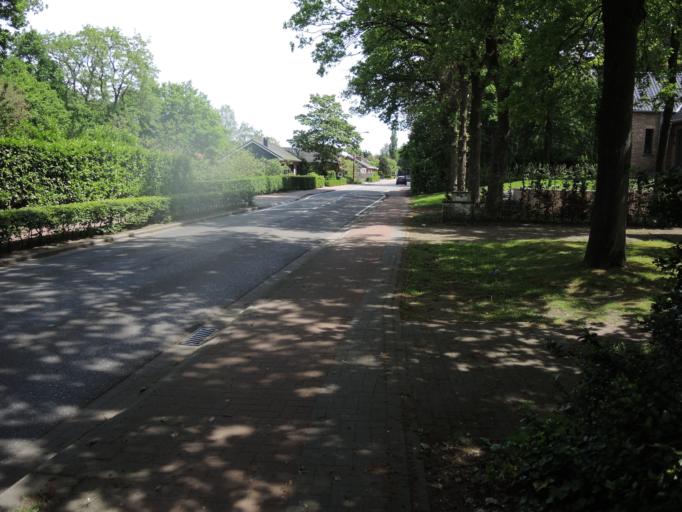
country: BE
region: Flanders
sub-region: Provincie Antwerpen
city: Kalmthout
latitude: 51.3704
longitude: 4.4870
